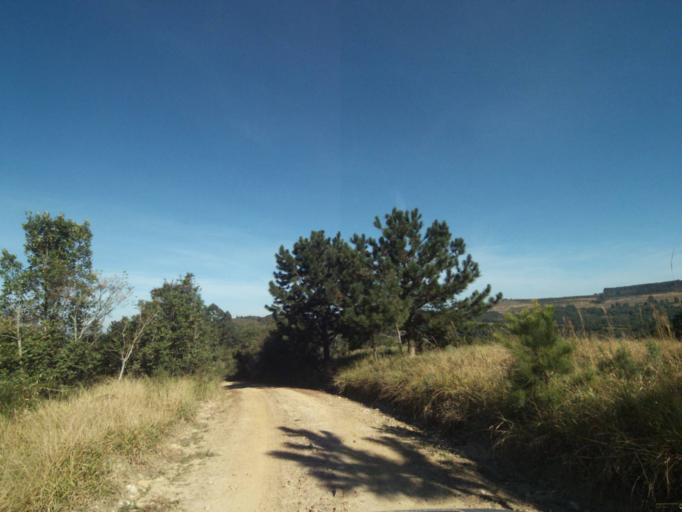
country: BR
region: Parana
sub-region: Tibagi
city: Tibagi
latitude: -24.5600
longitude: -50.4730
